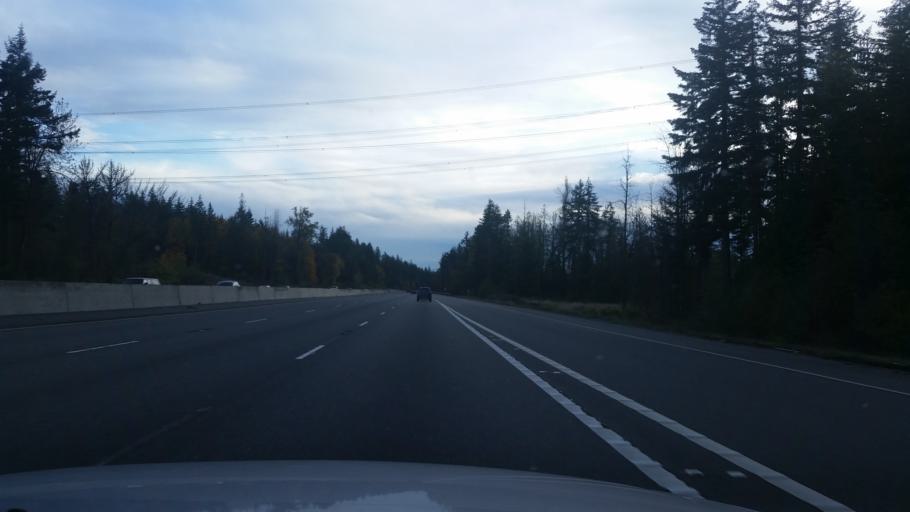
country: US
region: Washington
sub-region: Thurston County
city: Grand Mound
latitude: 46.8678
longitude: -122.9703
